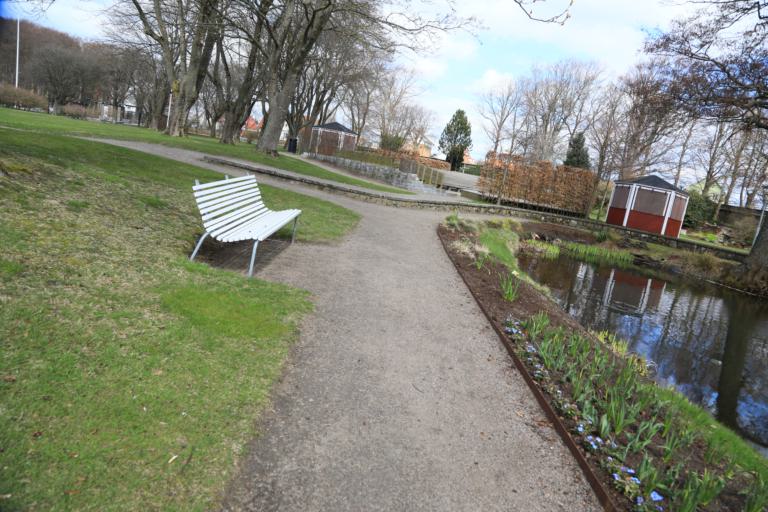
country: SE
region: Halland
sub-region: Varbergs Kommun
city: Varberg
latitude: 57.0996
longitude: 12.2650
